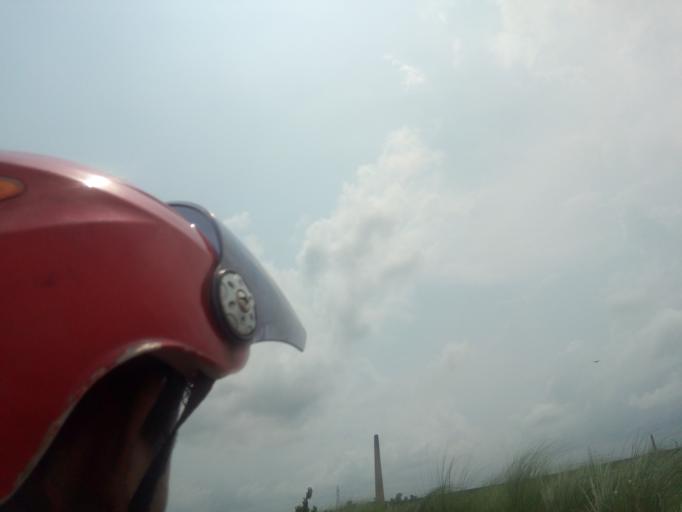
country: BD
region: Dhaka
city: Azimpur
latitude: 23.7504
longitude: 90.3330
